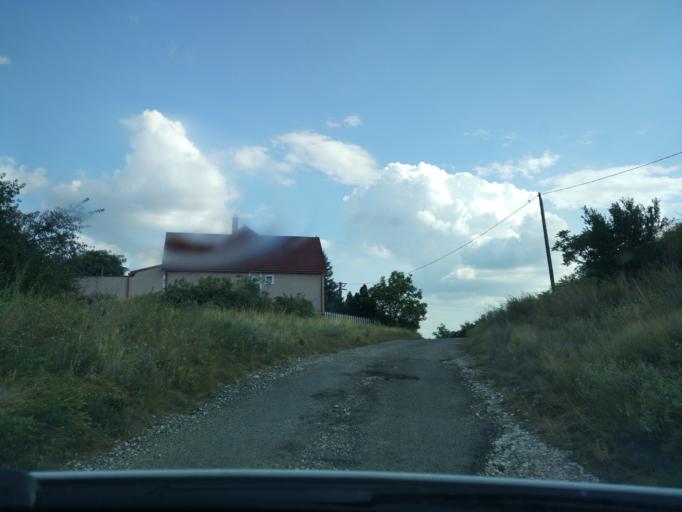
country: HU
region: Veszprem
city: Varpalota
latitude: 47.2045
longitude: 18.1757
